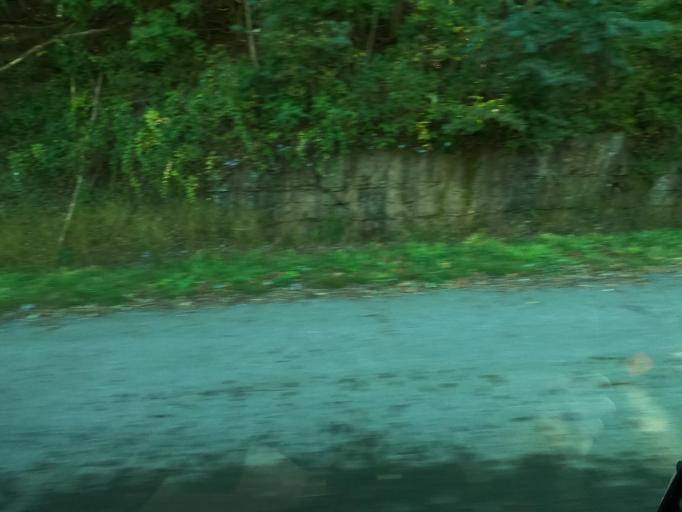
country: US
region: Tennessee
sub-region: Marion County
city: Monteagle
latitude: 35.2144
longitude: -85.7933
